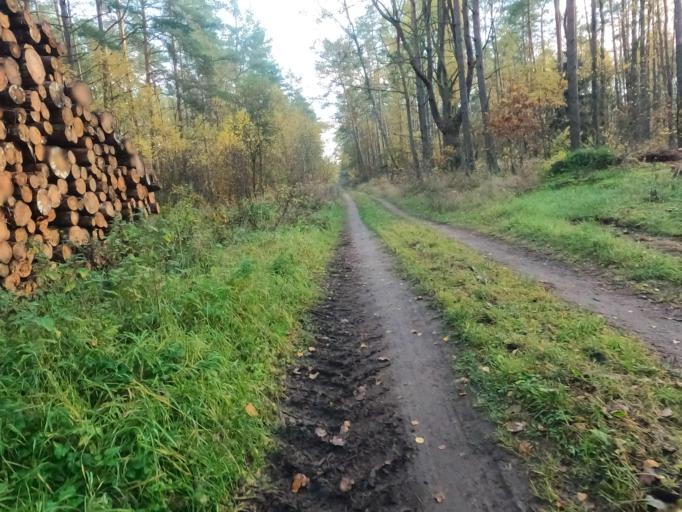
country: PL
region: West Pomeranian Voivodeship
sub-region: Powiat szczecinecki
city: Lubowo
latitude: 53.5770
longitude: 16.4039
